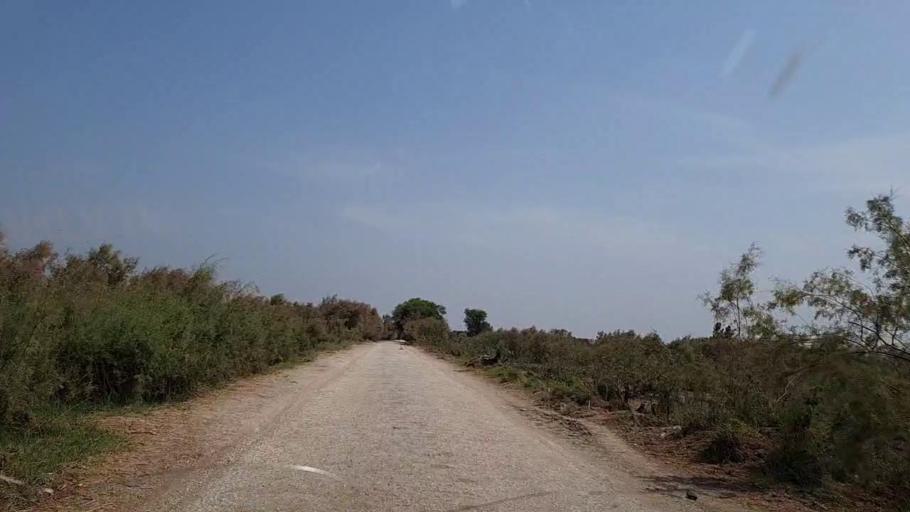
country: PK
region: Sindh
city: Khanpur
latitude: 27.8216
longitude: 69.3037
